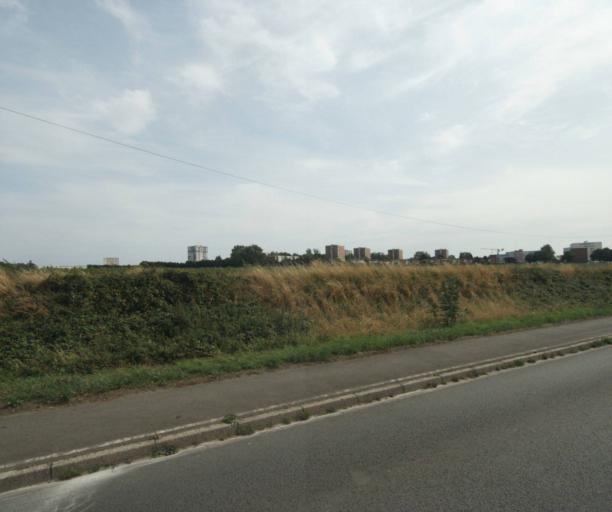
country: FR
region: Nord-Pas-de-Calais
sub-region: Departement du Nord
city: Wattignies
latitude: 50.5944
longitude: 3.0369
